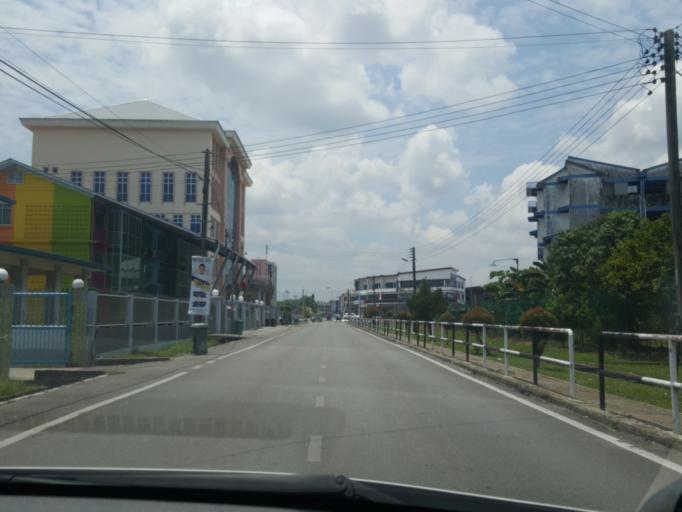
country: MY
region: Sarawak
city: Sarikei
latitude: 2.1288
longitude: 111.5205
